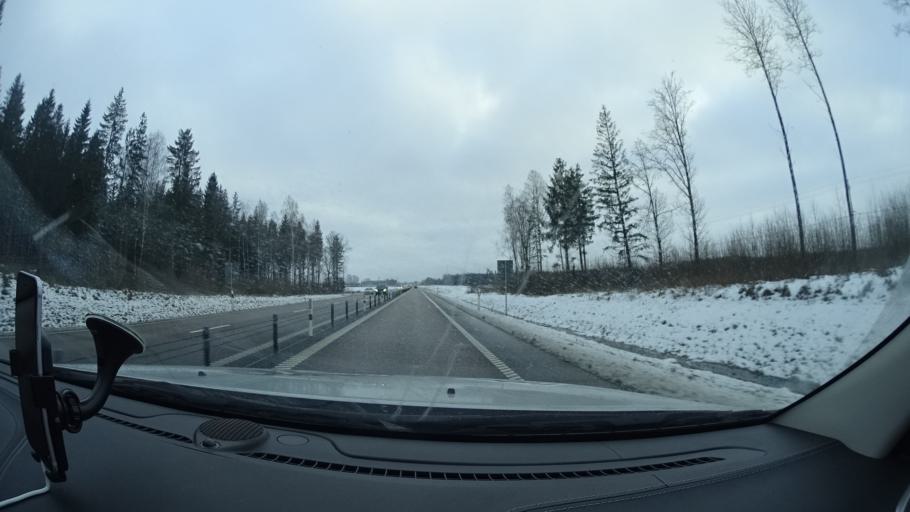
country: SE
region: OEstergoetland
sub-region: Motala Kommun
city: Stenstorp
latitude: 58.4260
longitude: 15.0675
